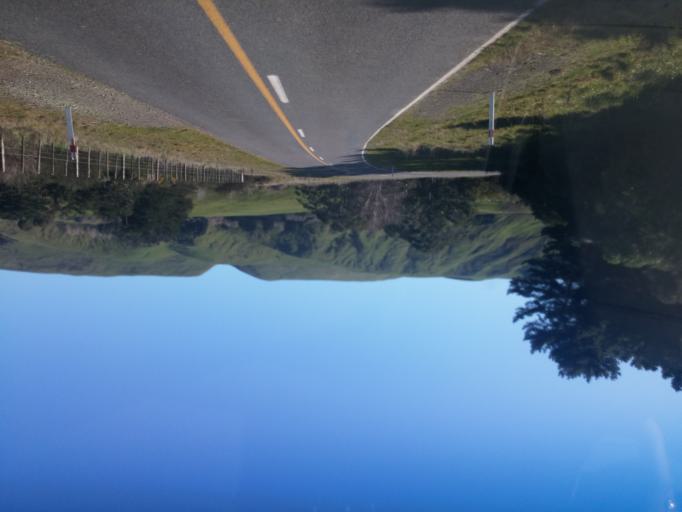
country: NZ
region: Wellington
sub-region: South Wairarapa District
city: Waipawa
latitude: -41.2968
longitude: 175.4685
